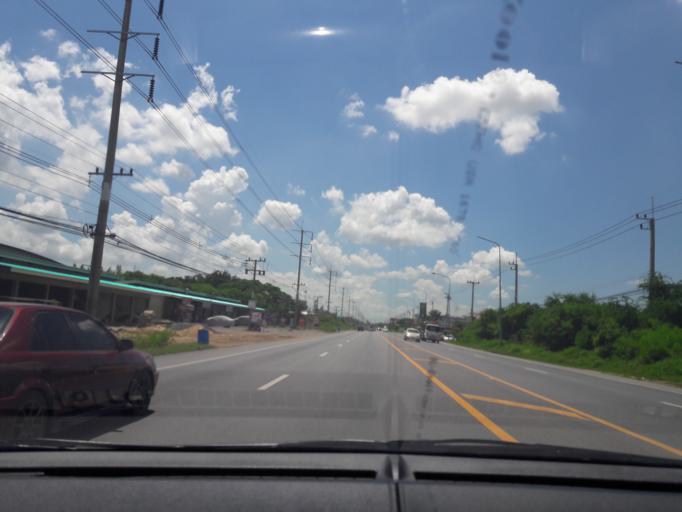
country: TH
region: Nakhon Pathom
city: Kamphaeng Saen
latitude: 14.0139
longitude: 100.0137
